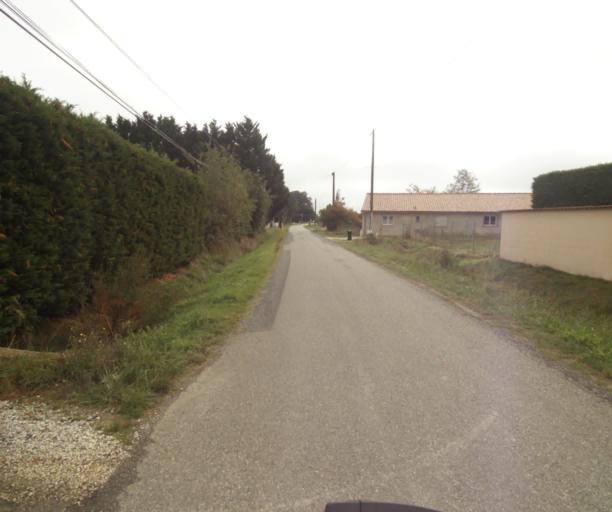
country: FR
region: Midi-Pyrenees
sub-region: Departement du Tarn-et-Garonne
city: Campsas
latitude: 43.8904
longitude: 1.3423
